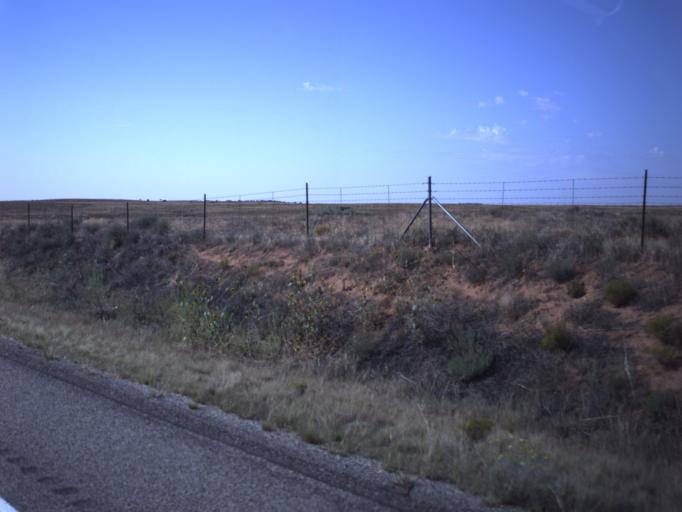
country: US
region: Utah
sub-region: San Juan County
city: Blanding
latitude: 37.4528
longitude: -109.4671
